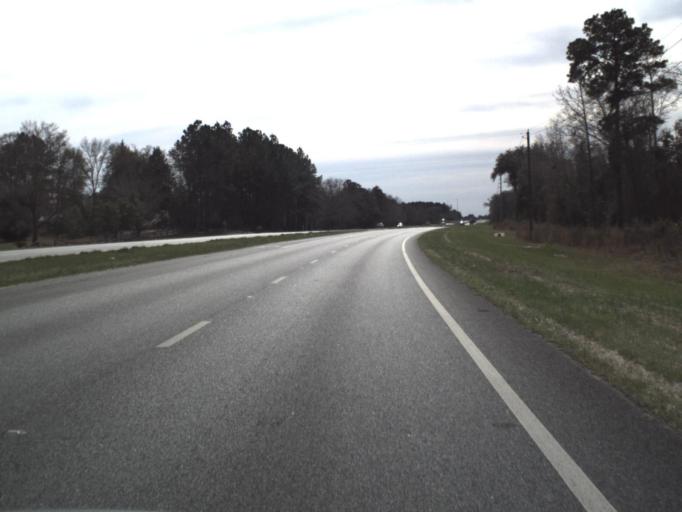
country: US
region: Florida
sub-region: Jackson County
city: Marianna
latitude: 30.7689
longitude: -85.3747
